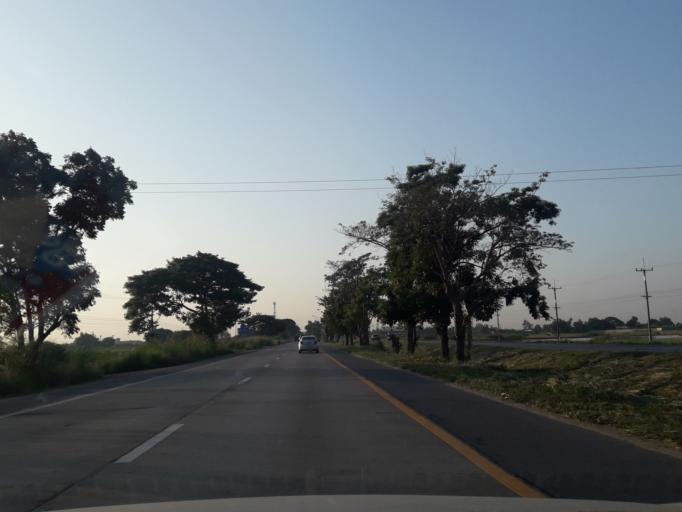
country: TH
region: Phra Nakhon Si Ayutthaya
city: Bang Pa-in
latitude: 14.2698
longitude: 100.5314
